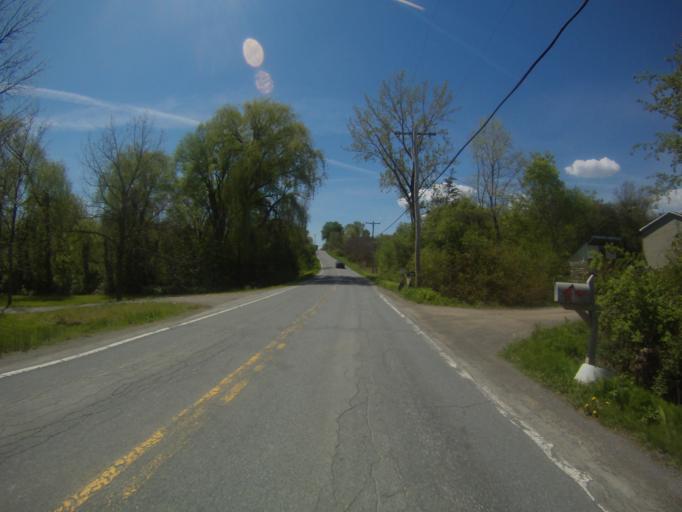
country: US
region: New York
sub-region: Essex County
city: Port Henry
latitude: 43.9800
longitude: -73.4217
